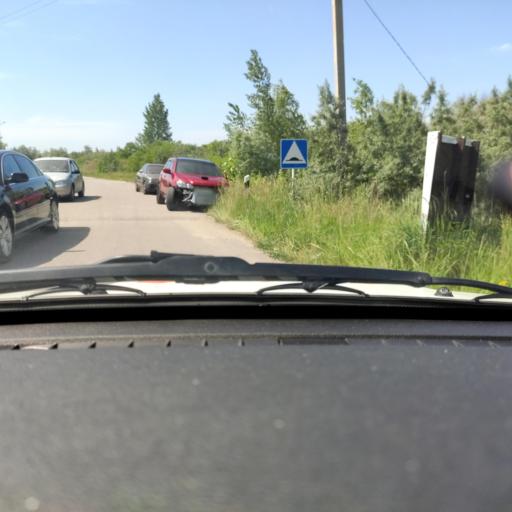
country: RU
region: Voronezj
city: Devitsa
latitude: 51.6231
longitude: 38.9598
